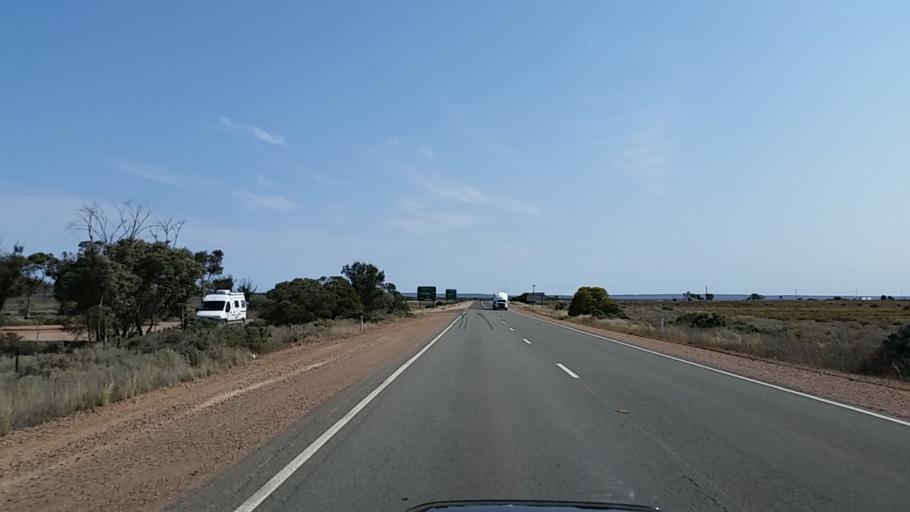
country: AU
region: South Australia
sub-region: Port Augusta
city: Port Augusta West
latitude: -32.6158
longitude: 137.5740
